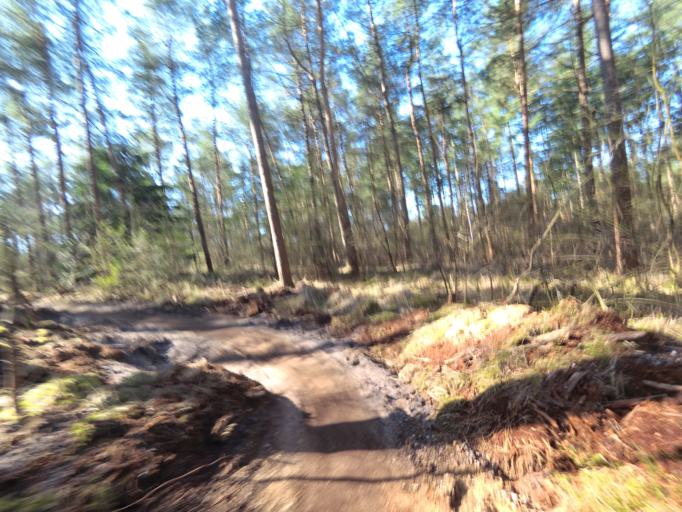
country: NL
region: Utrecht
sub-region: Gemeente Utrechtse Heuvelrug
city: Maarn
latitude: 52.0927
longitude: 5.3405
